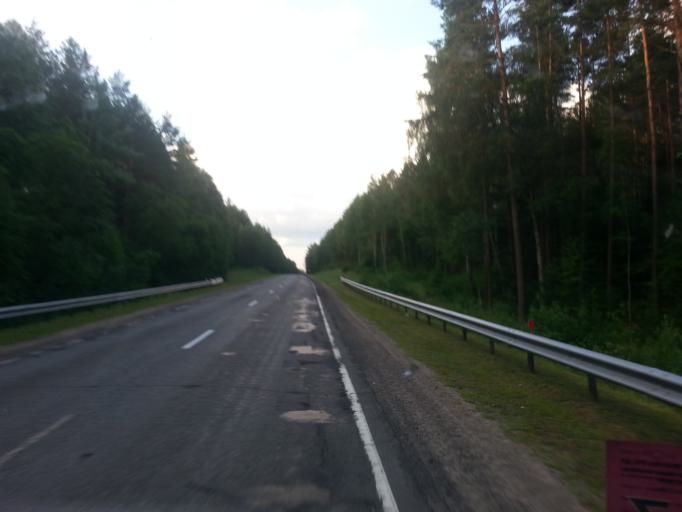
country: BY
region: Minsk
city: Kryvichy
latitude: 54.5676
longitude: 27.2071
